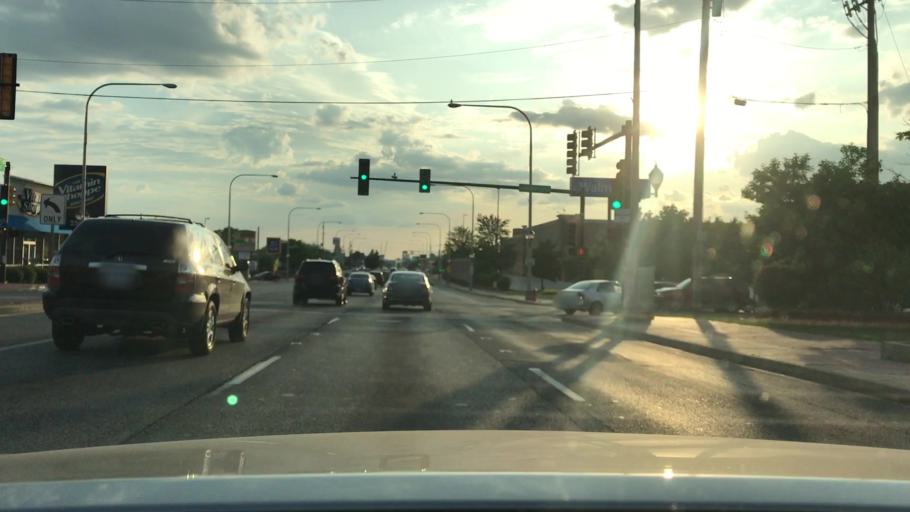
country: US
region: Illinois
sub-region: Cook County
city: Evergreen Park
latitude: 41.7210
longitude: -87.6841
